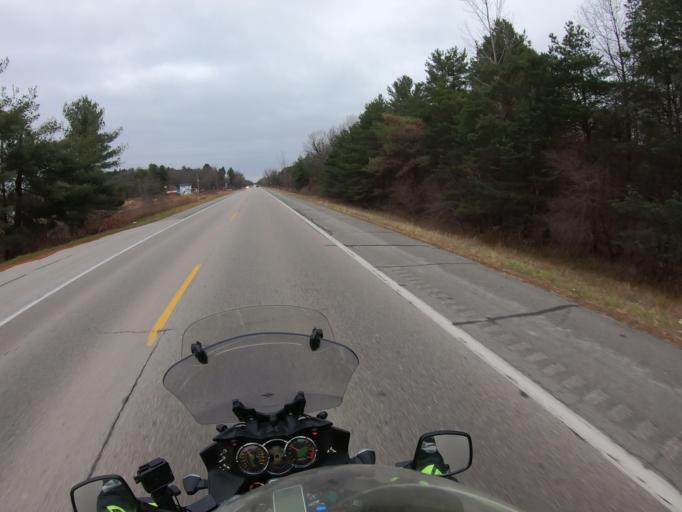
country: US
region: Michigan
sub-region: Saginaw County
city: Saint Charles
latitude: 43.3176
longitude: -84.1418
